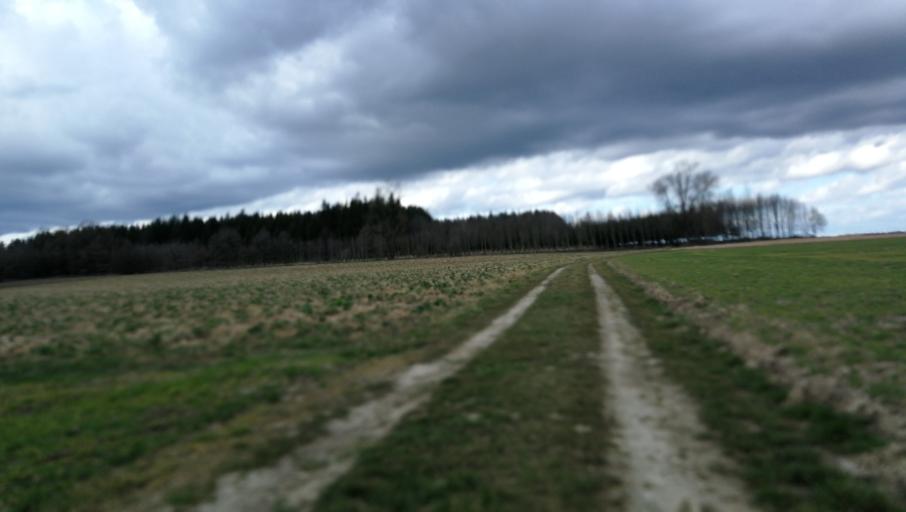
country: DE
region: Bavaria
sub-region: Upper Bavaria
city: Fuerstenfeldbruck
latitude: 48.1967
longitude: 11.2099
